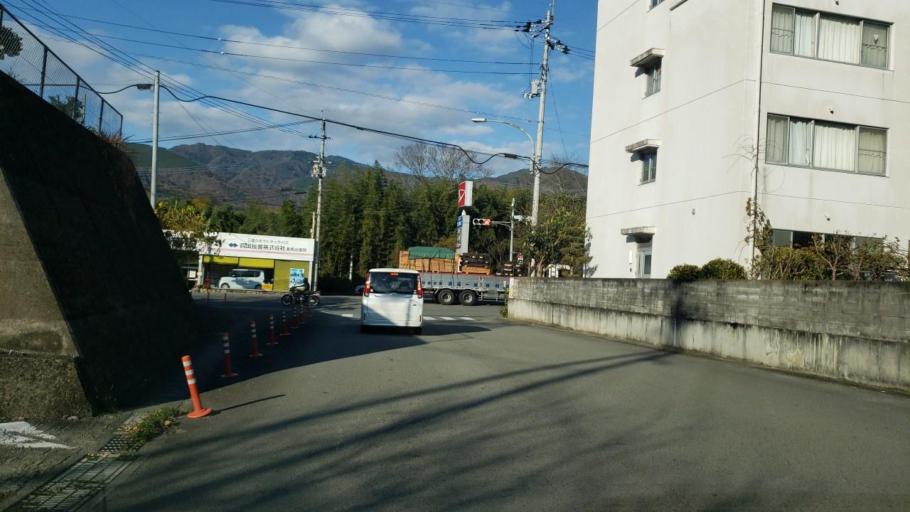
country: JP
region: Tokushima
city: Wakimachi
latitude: 34.0416
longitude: 134.0287
